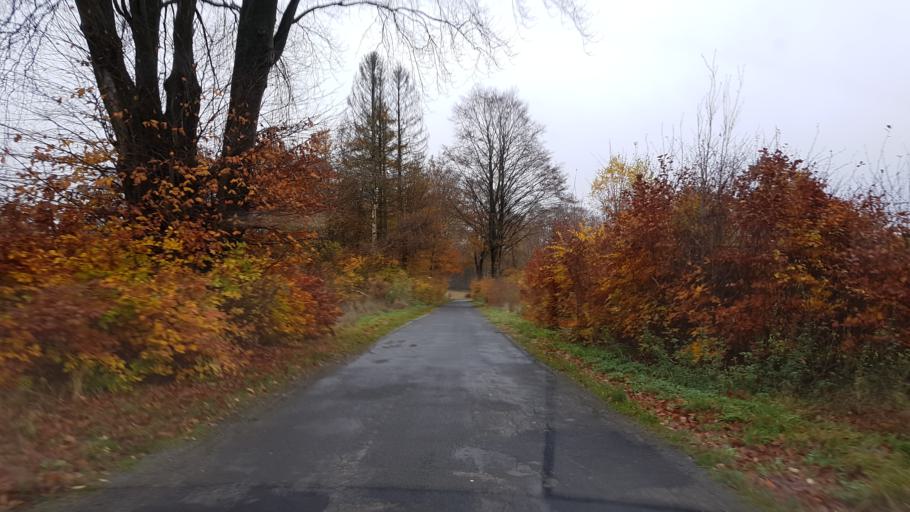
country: PL
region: West Pomeranian Voivodeship
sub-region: Powiat koszalinski
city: Polanow
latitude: 54.0852
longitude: 16.5944
